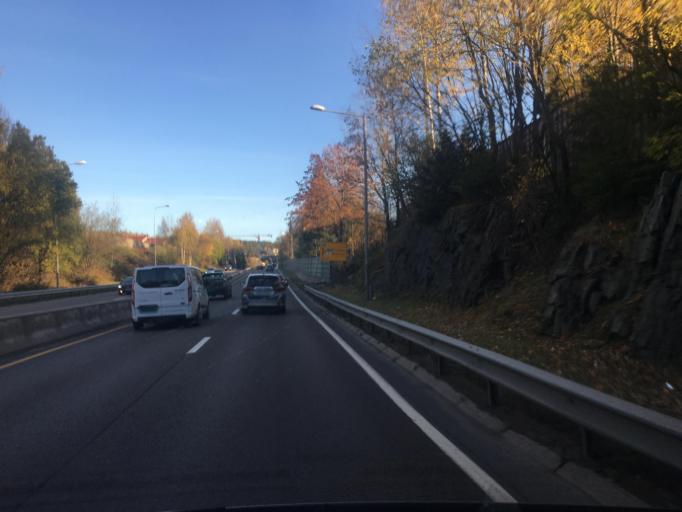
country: NO
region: Akershus
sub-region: Lorenskog
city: Kjenn
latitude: 59.9501
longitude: 10.9383
